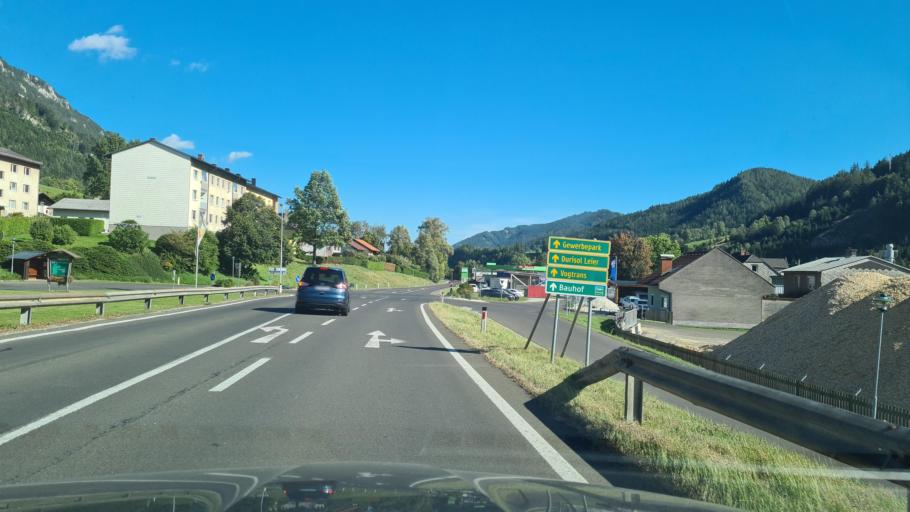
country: AT
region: Styria
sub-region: Politischer Bezirk Leoben
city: Mautern in Steiermark
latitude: 47.3981
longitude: 14.8334
